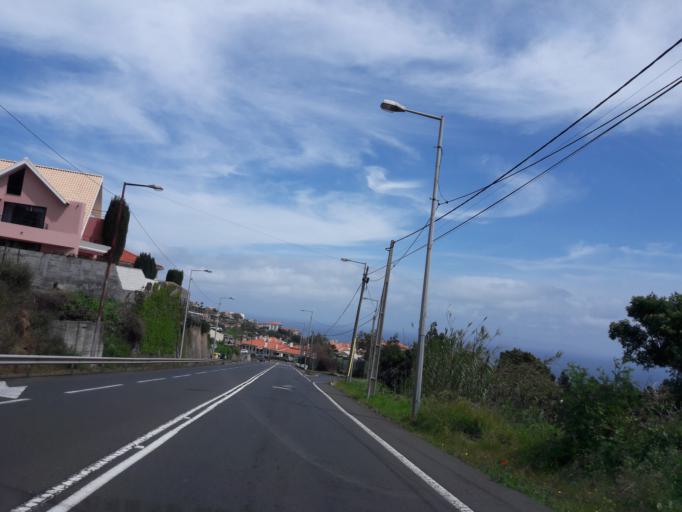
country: PT
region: Madeira
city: Canico
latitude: 32.6536
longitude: -16.8459
